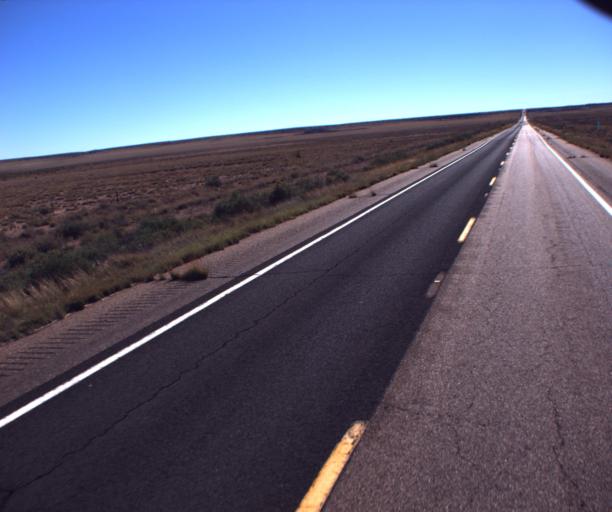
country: US
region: Arizona
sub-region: Navajo County
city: Snowflake
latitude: 34.7393
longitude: -109.7908
